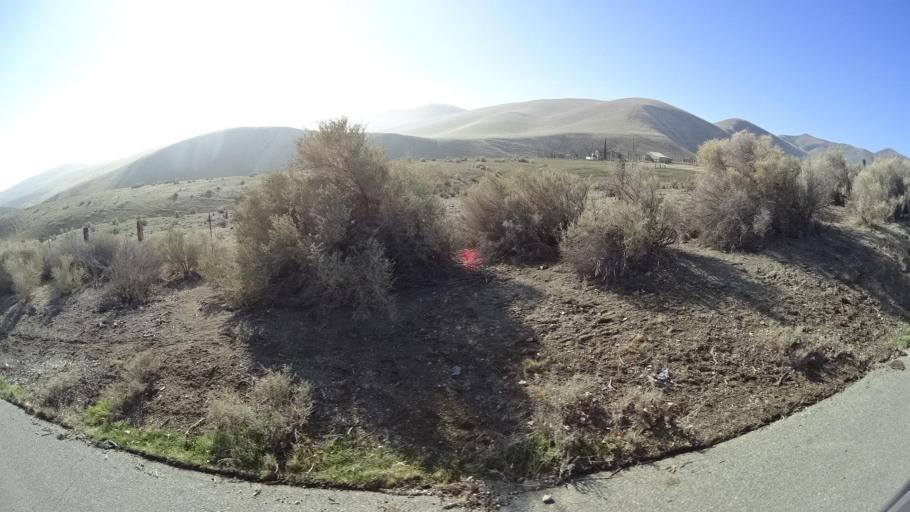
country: US
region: California
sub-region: Kern County
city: Taft Heights
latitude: 35.2340
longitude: -119.6583
